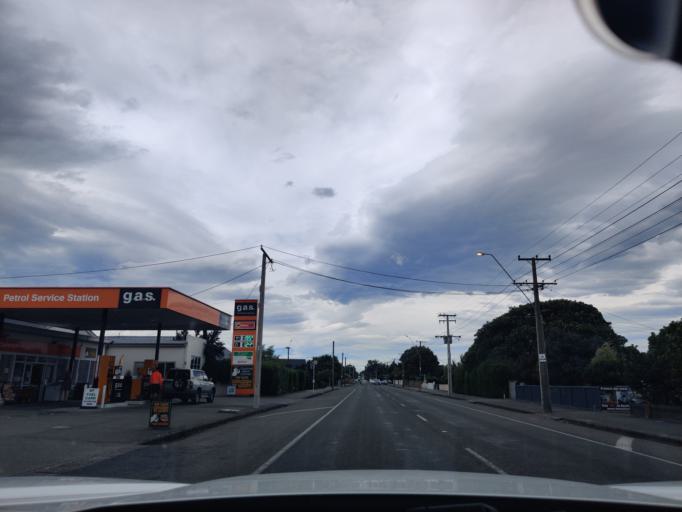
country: NZ
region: Wellington
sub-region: Masterton District
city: Masterton
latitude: -41.0331
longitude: 175.5197
